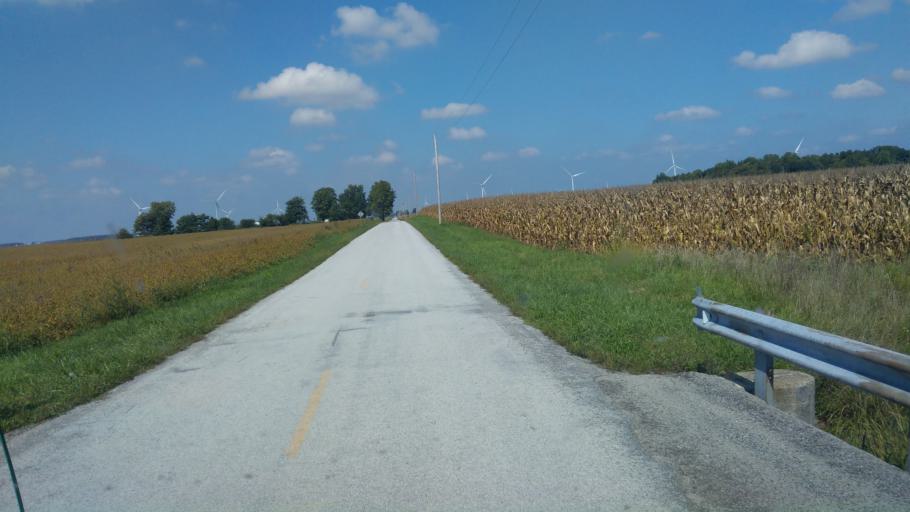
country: US
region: Ohio
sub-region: Hardin County
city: Ada
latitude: 40.7482
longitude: -83.7288
